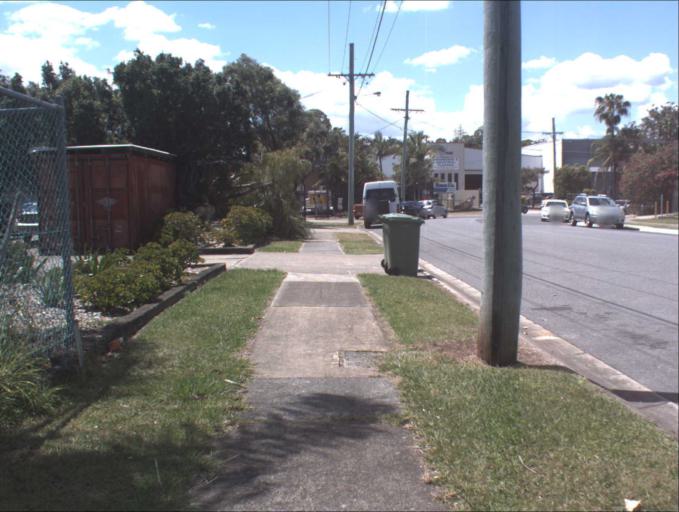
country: AU
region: Queensland
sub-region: Logan
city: Rochedale South
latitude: -27.6065
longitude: 153.1139
